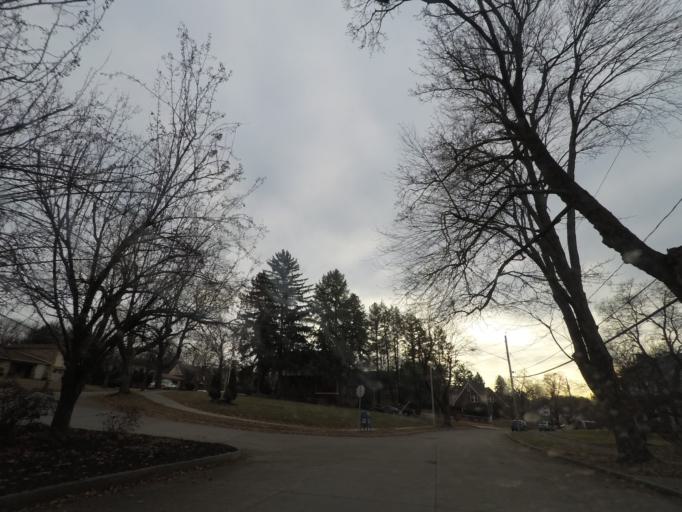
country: US
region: New York
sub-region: Albany County
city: Green Island
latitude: 42.7410
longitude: -73.6664
